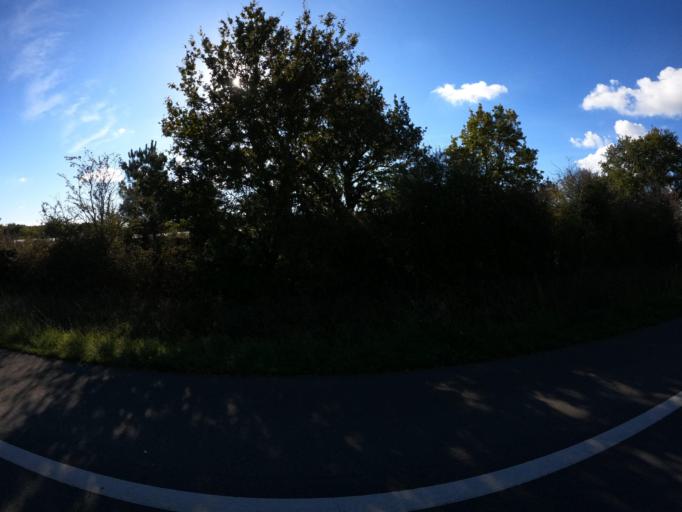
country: FR
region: Pays de la Loire
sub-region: Departement de la Loire-Atlantique
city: Saint-Andre-des-Eaux
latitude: 47.2860
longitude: -2.3120
